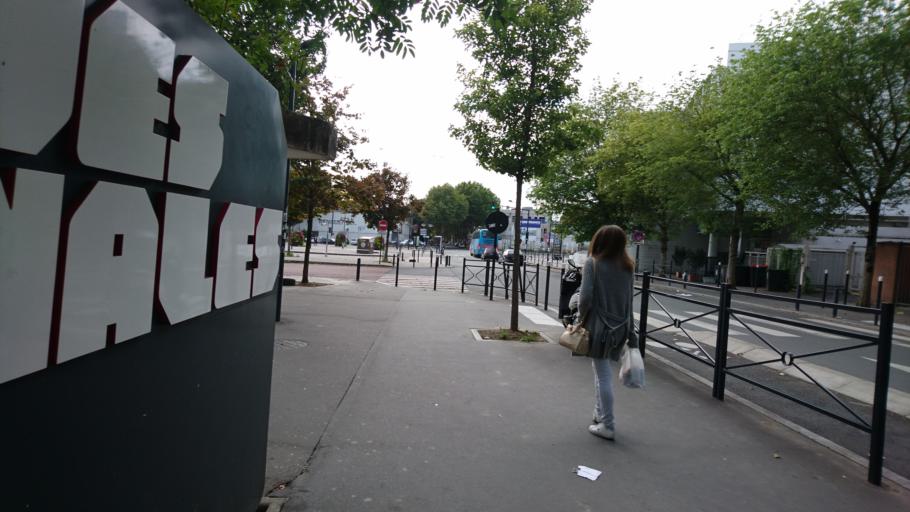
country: FR
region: Ile-de-France
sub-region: Departement de Seine-Saint-Denis
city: Saint-Denis
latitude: 48.9462
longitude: 2.3630
